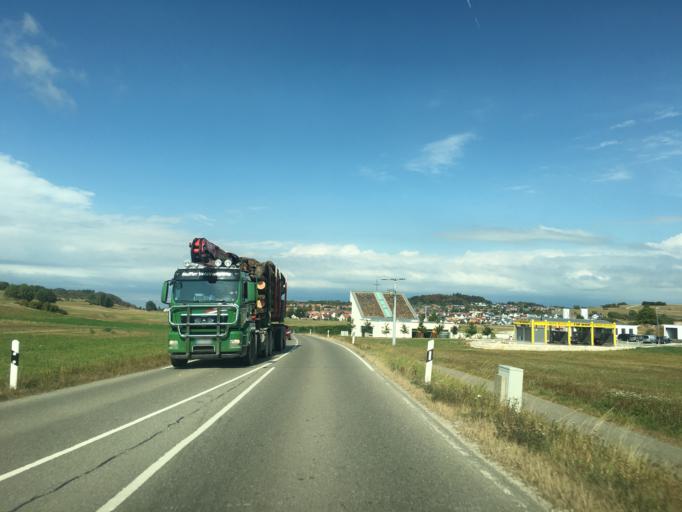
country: DE
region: Baden-Wuerttemberg
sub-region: Tuebingen Region
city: Pfullingen
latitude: 48.3947
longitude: 9.1820
